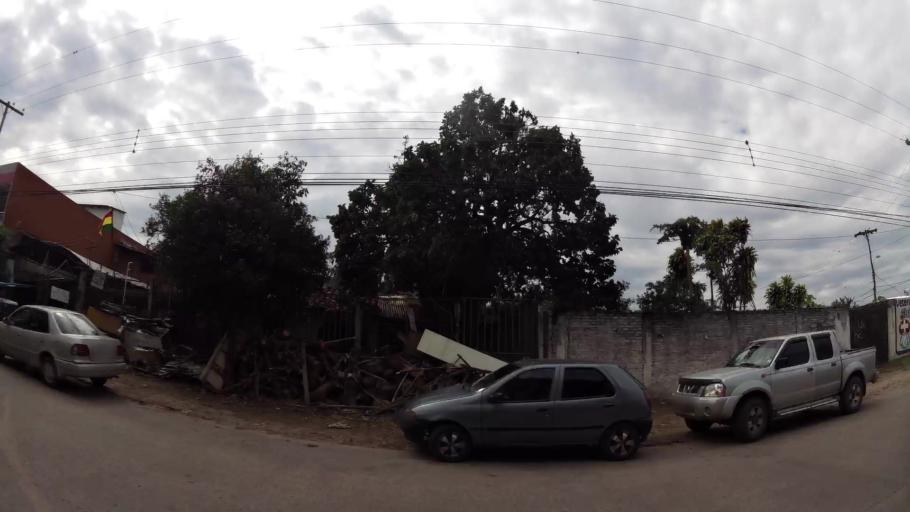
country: BO
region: Santa Cruz
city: Santa Cruz de la Sierra
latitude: -17.7541
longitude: -63.1903
